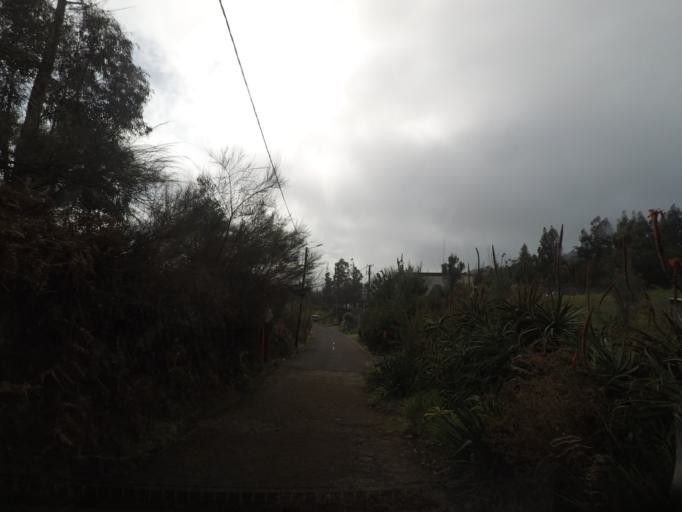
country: PT
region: Madeira
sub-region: Calheta
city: Estreito da Calheta
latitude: 32.7504
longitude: -17.1870
